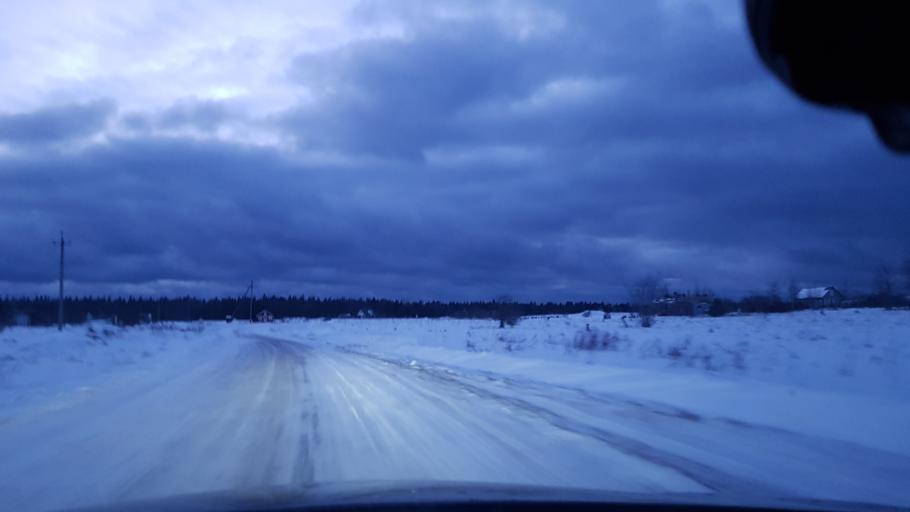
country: EE
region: Laeaene
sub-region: Haapsalu linn
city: Haapsalu
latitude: 59.2201
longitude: 23.5257
